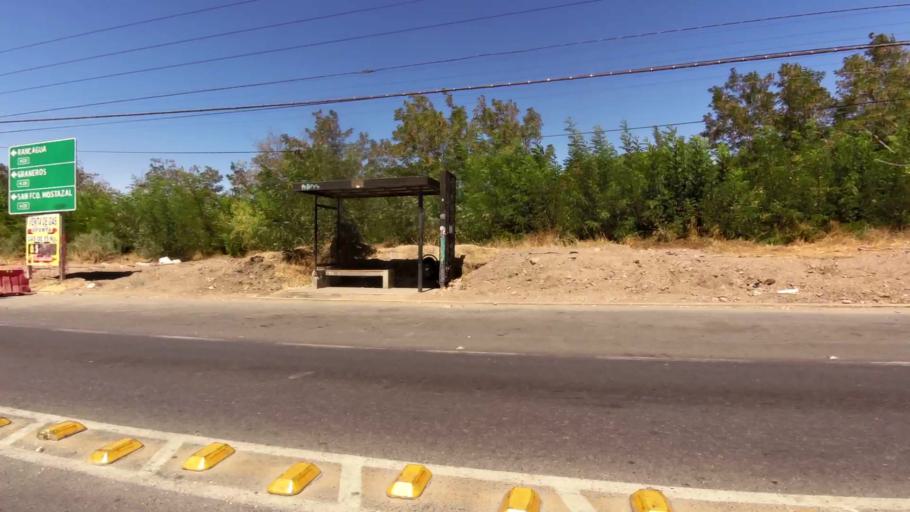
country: CL
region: O'Higgins
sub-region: Provincia de Cachapoal
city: Rancagua
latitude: -34.1712
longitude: -70.7771
